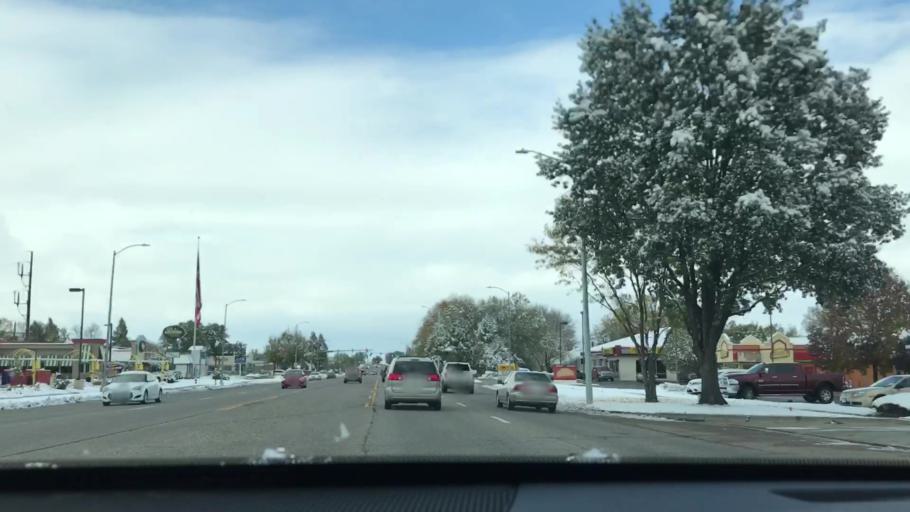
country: US
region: Colorado
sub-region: Boulder County
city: Longmont
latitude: 40.1937
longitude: -105.1023
